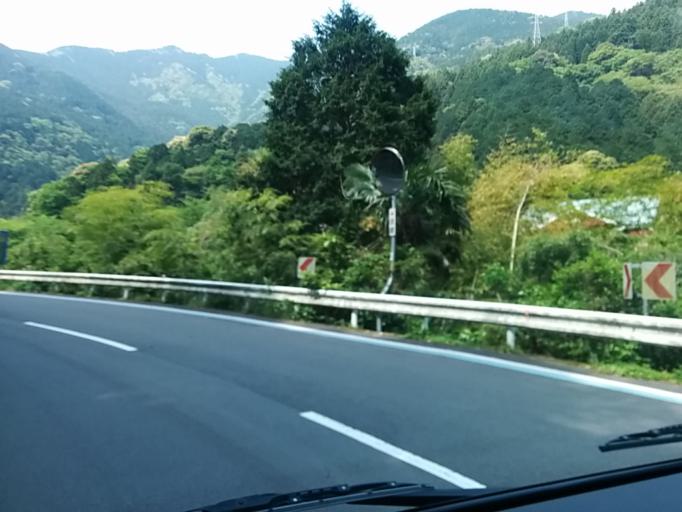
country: JP
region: Ehime
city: Niihama
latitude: 33.9012
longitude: 133.3106
